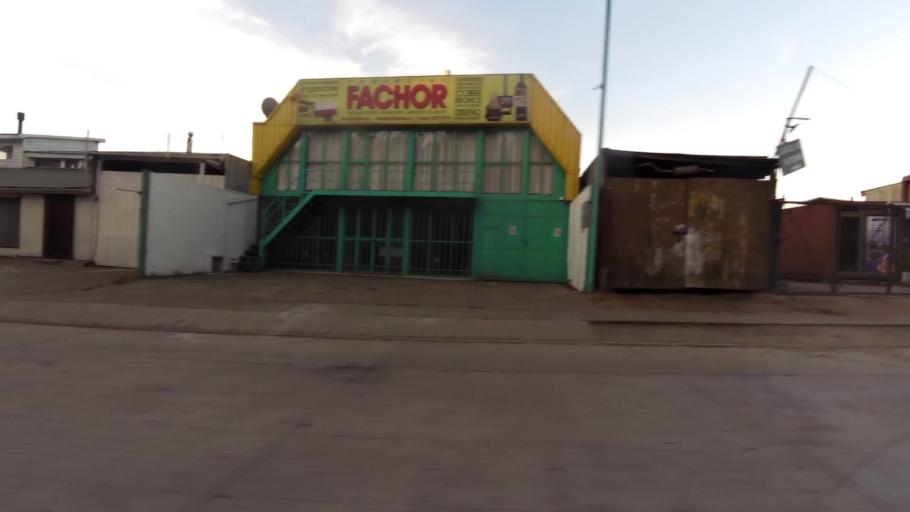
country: CL
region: Biobio
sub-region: Provincia de Concepcion
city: Concepcion
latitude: -36.8392
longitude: -73.0868
